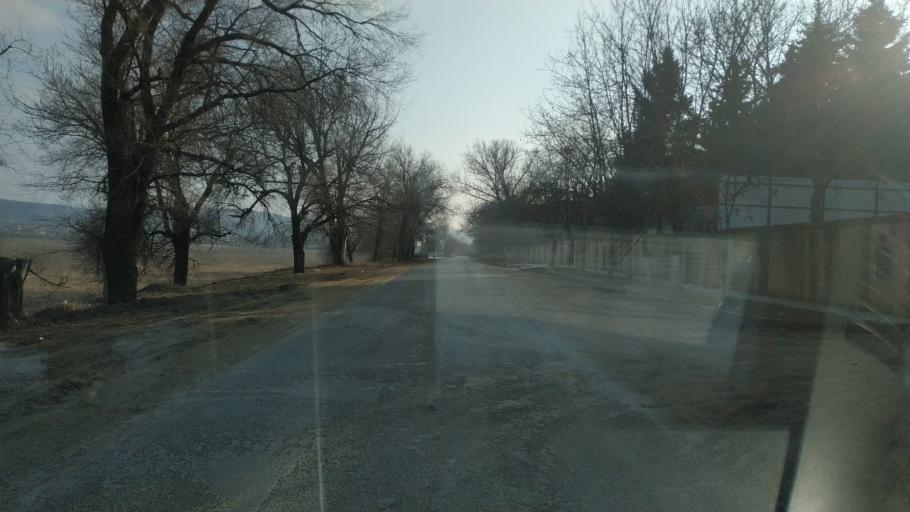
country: MD
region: Hincesti
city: Dancu
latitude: 46.7706
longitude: 28.3463
